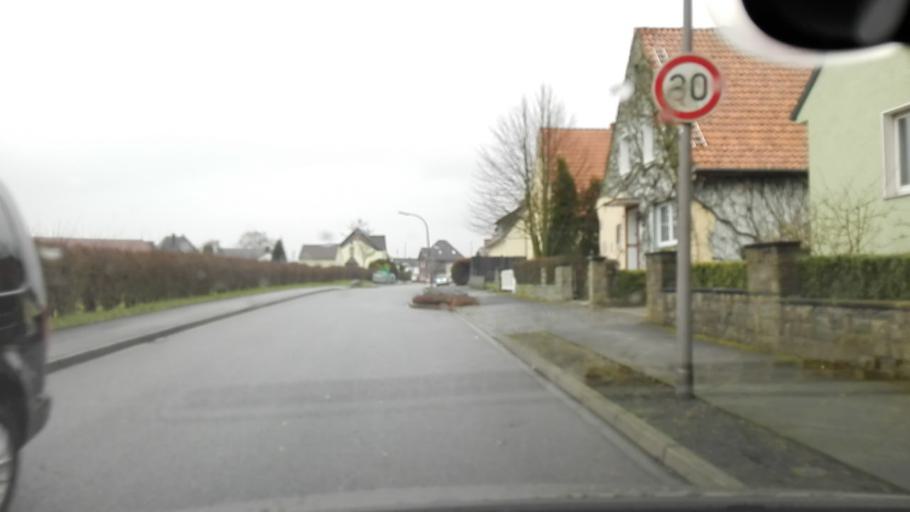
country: DE
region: North Rhine-Westphalia
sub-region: Regierungsbezirk Arnsberg
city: Bonen
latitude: 51.5806
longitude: 7.7236
